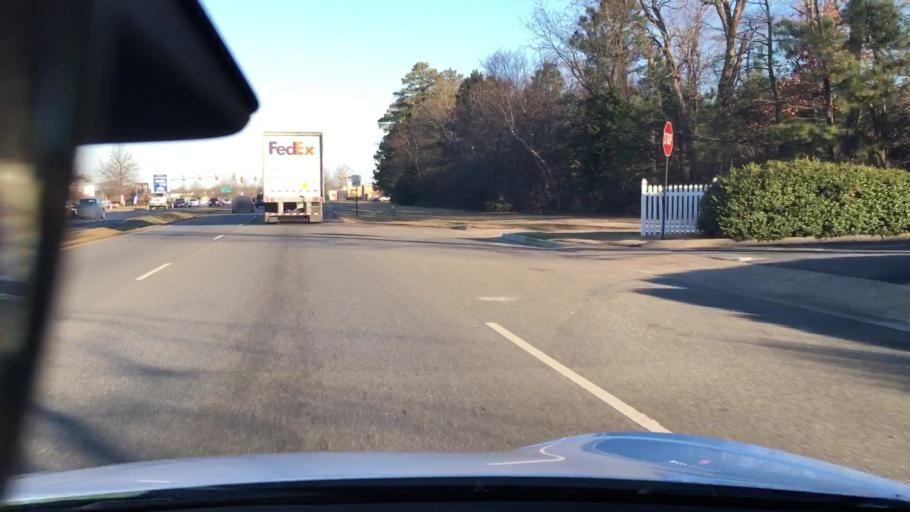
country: US
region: Virginia
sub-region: Henrico County
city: Montrose
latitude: 37.5220
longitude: -77.3519
